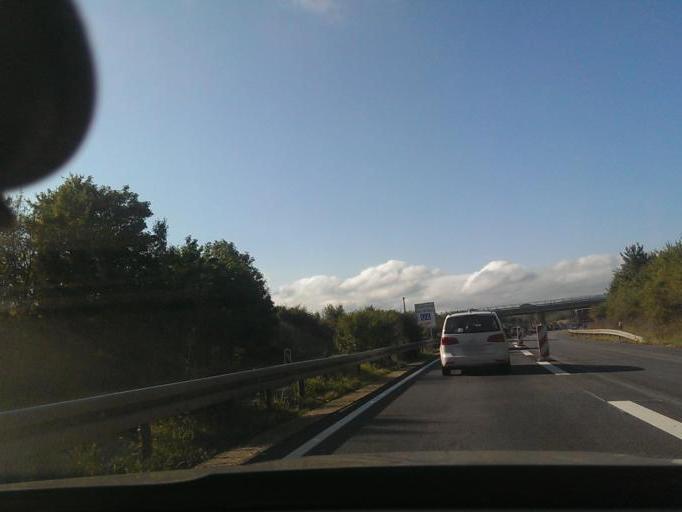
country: DE
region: Lower Saxony
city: Vienenburg
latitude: 51.9426
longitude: 10.5853
